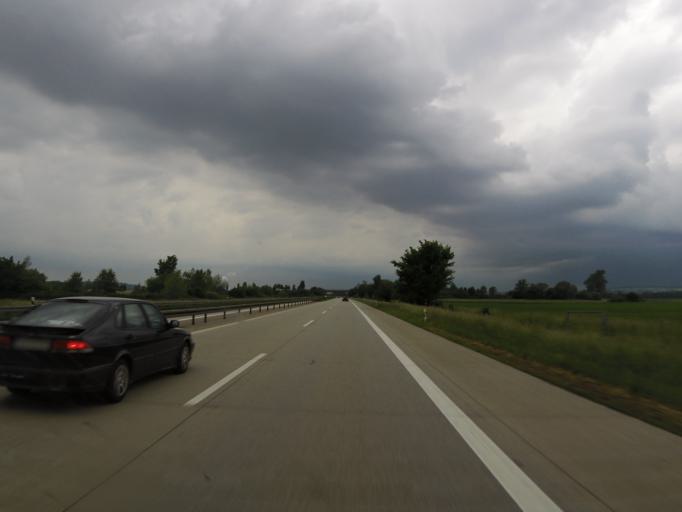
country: DE
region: Bavaria
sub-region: Lower Bavaria
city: Loiching
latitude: 48.6431
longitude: 12.4123
